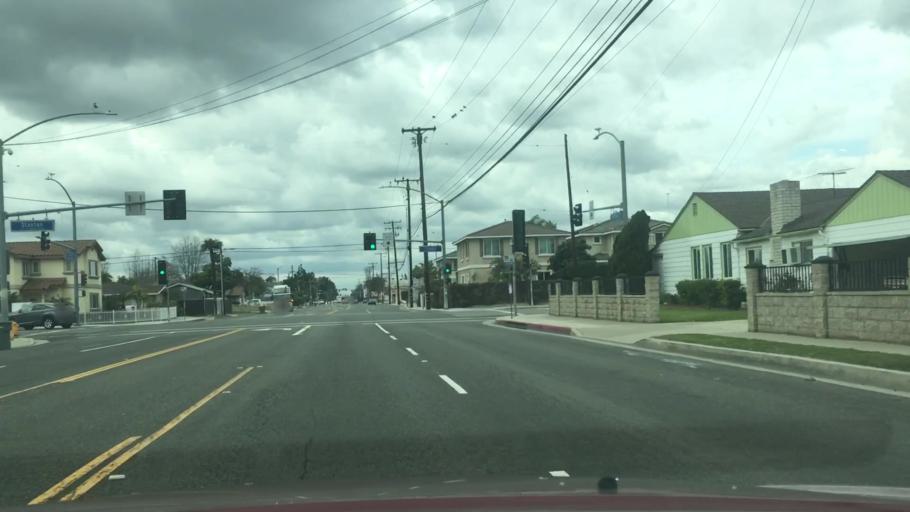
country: US
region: California
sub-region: Orange County
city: Buena Park
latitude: 33.8736
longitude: -117.9934
